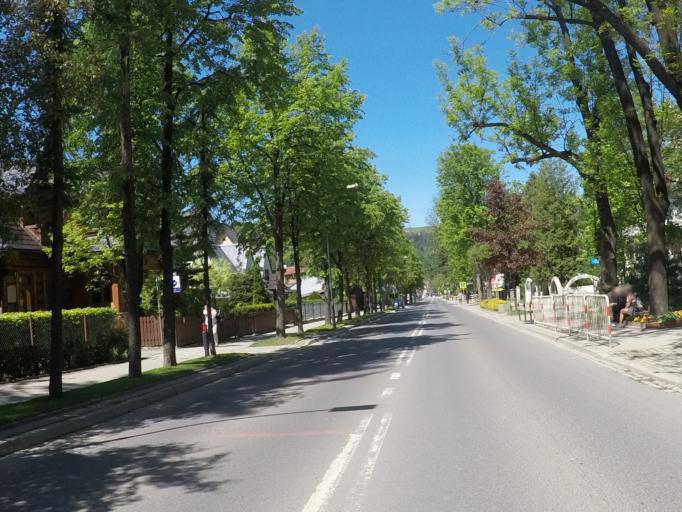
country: PL
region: Lesser Poland Voivodeship
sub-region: Powiat tatrzanski
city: Zakopane
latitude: 49.3019
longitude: 19.9607
